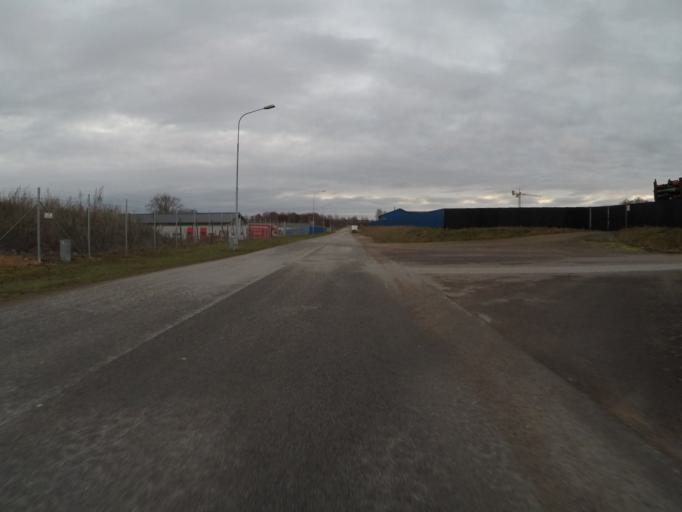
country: SE
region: Skane
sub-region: Sjobo Kommun
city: Sjoebo
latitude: 55.6368
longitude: 13.6876
